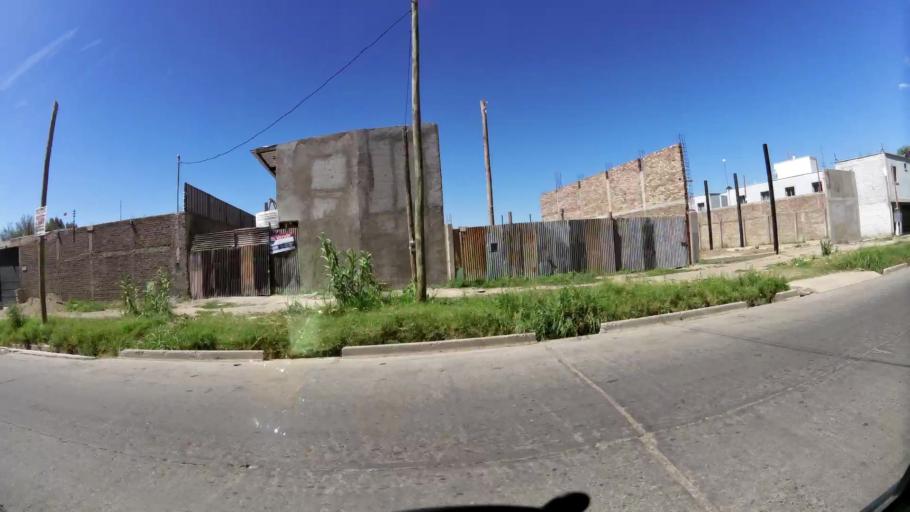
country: AR
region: Mendoza
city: Las Heras
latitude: -32.8451
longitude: -68.8468
